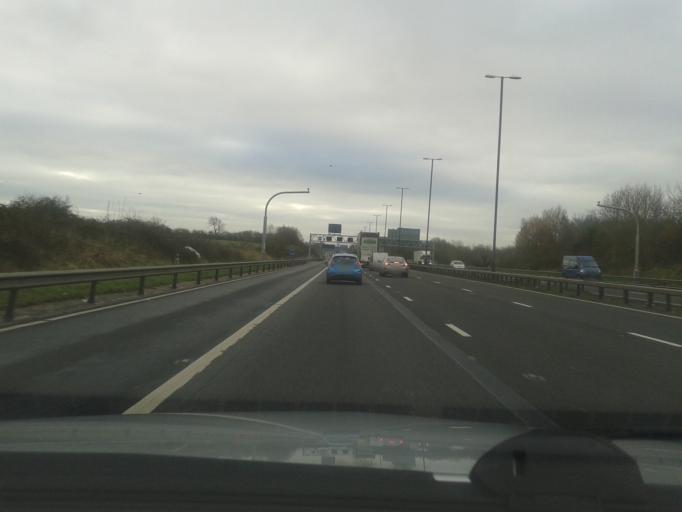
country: GB
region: England
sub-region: South Gloucestershire
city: Stoke Gifford
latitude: 51.5389
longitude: -2.5410
